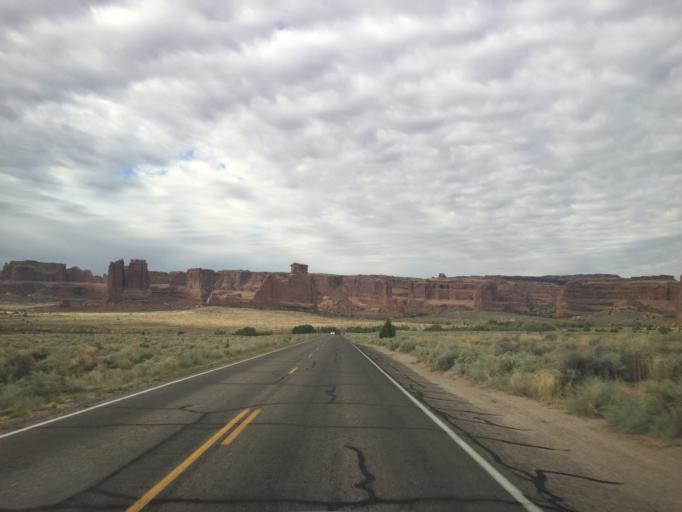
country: US
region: Utah
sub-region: Grand County
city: Moab
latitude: 38.6538
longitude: -109.5942
